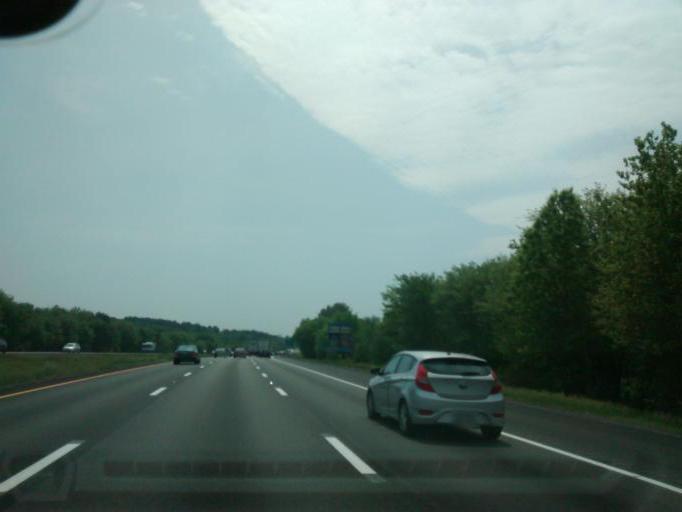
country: US
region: Massachusetts
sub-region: Norfolk County
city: Bellingham
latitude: 42.0996
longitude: -71.4388
